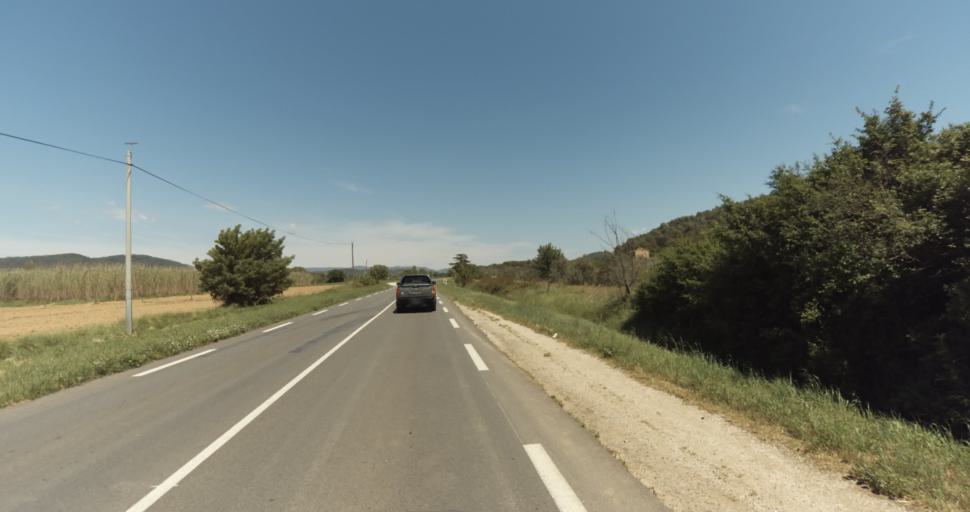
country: FR
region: Provence-Alpes-Cote d'Azur
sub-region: Departement du Var
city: Pierrefeu-du-Var
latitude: 43.1812
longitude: 6.1188
